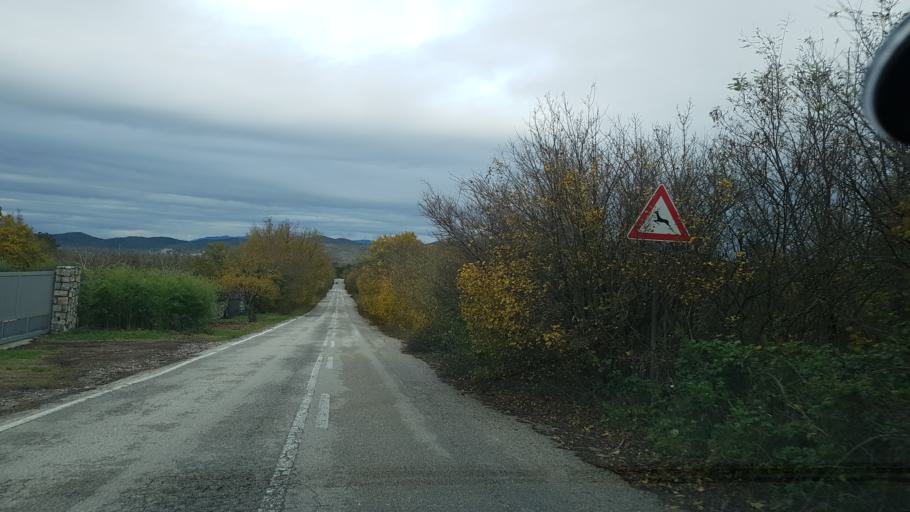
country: IT
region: Friuli Venezia Giulia
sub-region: Provincia di Trieste
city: Prosecco-Contovello
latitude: 45.7004
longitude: 13.7428
